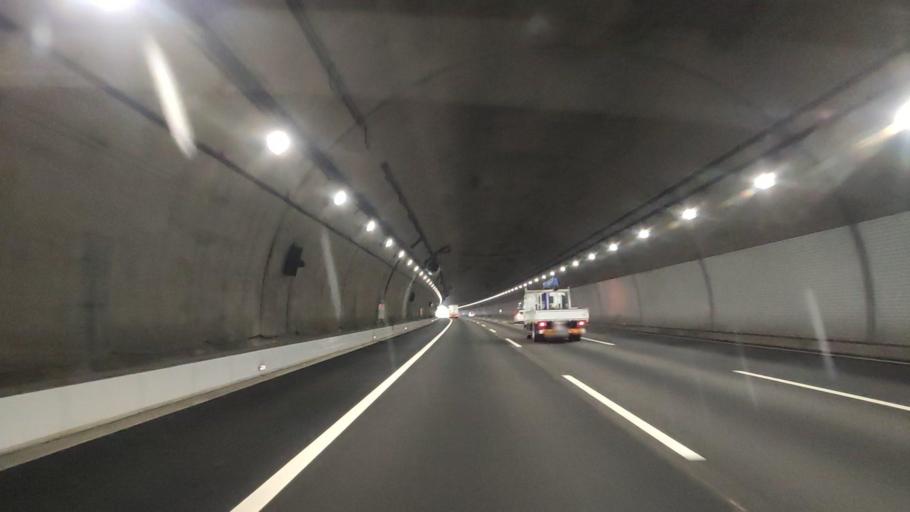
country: JP
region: Shizuoka
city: Shizuoka-shi
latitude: 35.0626
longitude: 138.4409
